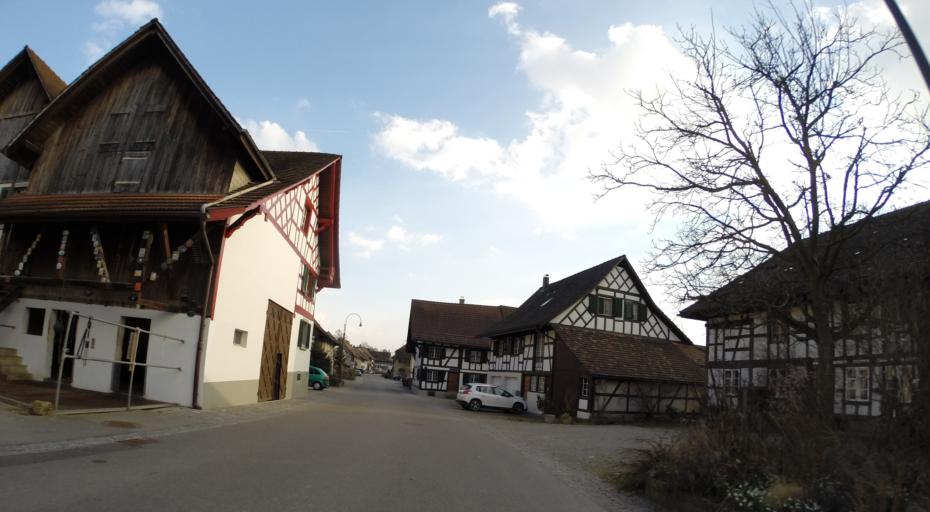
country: CH
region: Thurgau
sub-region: Frauenfeld District
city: Wagenhausen
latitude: 47.6386
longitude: 8.7904
